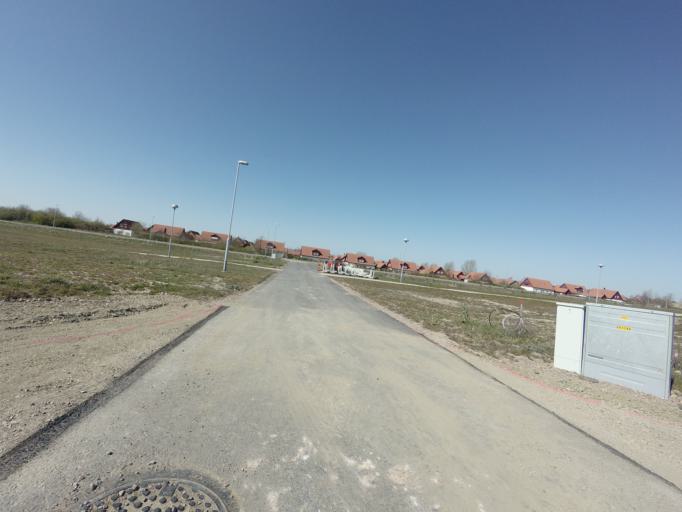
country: SE
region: Skane
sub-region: Vellinge Kommun
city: Vellinge
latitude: 55.4718
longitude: 13.0419
